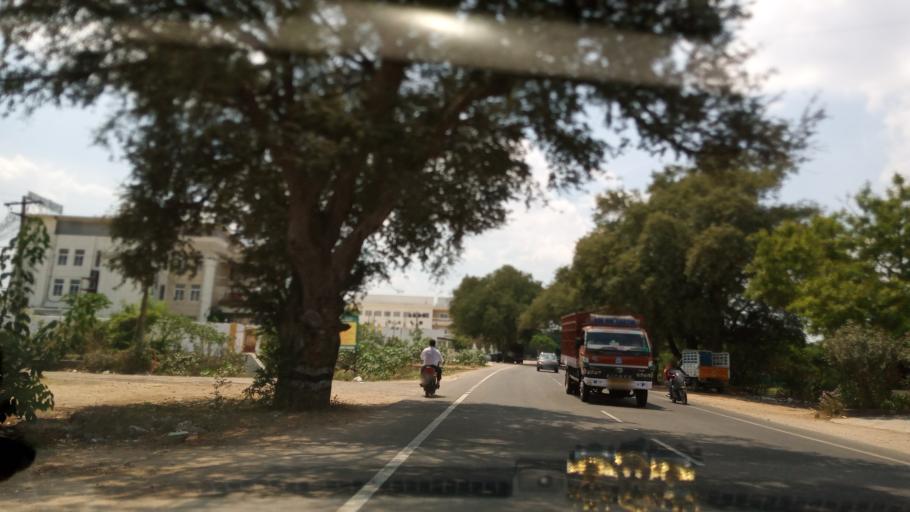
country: IN
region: Tamil Nadu
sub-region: Vellore
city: Walajapet
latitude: 12.9199
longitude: 79.3811
